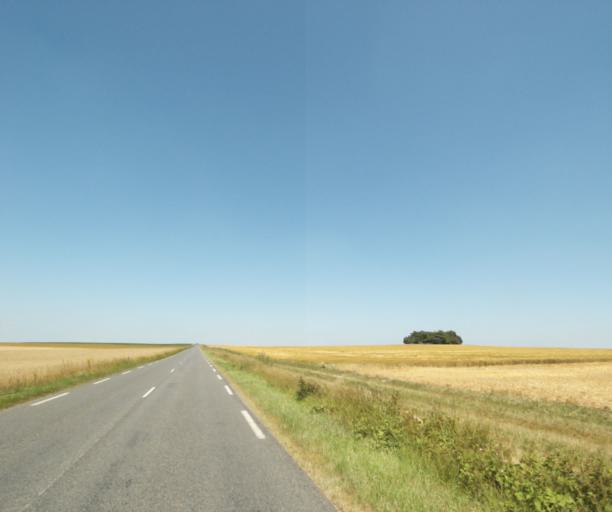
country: FR
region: Centre
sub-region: Departement du Loiret
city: Malesherbes
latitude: 48.3185
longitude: 2.4421
